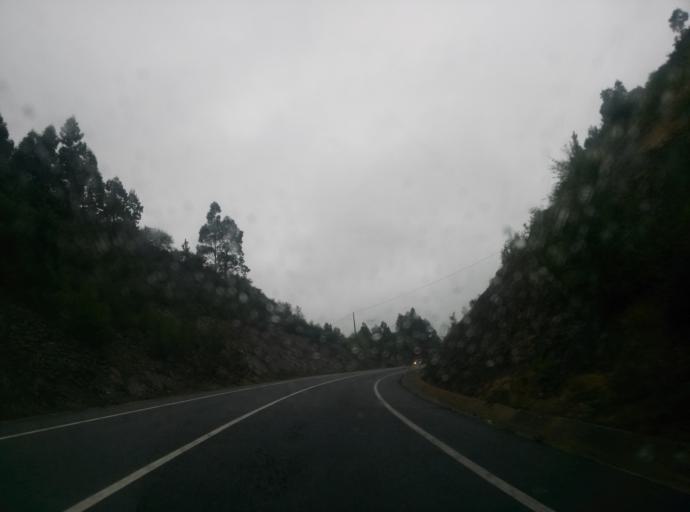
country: ES
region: Galicia
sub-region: Provincia de Lugo
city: Muras
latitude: 43.5539
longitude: -7.6492
